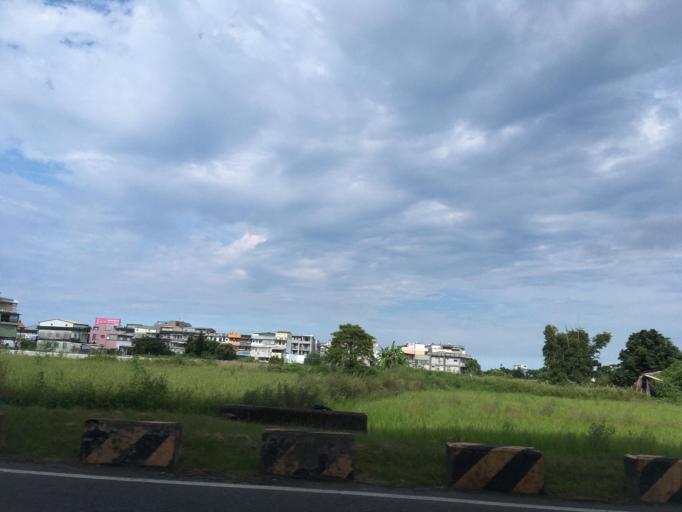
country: TW
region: Taiwan
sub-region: Yilan
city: Yilan
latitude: 24.6828
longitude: 121.7928
